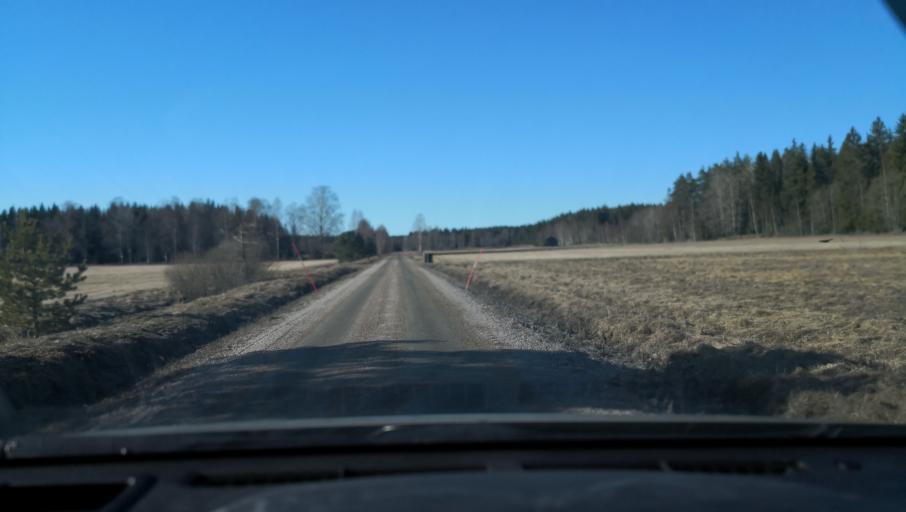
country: SE
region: Vaestmanland
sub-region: Sala Kommun
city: Sala
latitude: 60.1265
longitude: 16.6552
